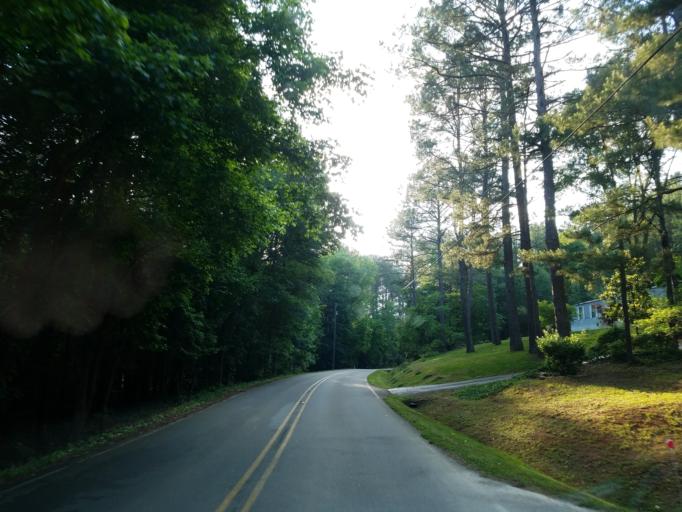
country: US
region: Georgia
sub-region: Cherokee County
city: Ball Ground
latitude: 34.3003
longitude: -84.3851
